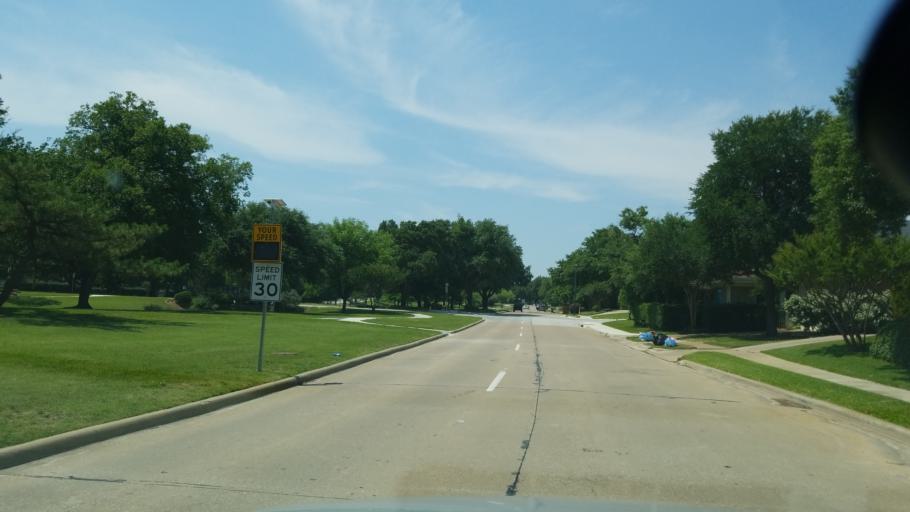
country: US
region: Texas
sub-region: Dallas County
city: Irving
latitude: 32.8500
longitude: -96.9359
